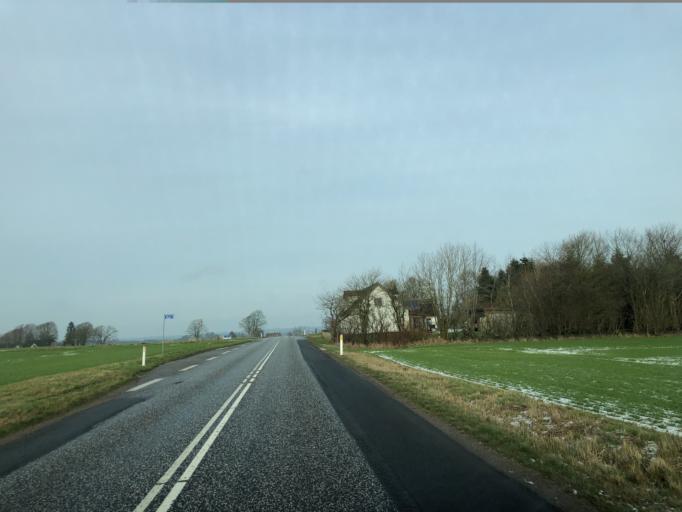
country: DK
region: Central Jutland
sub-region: Hedensted Kommune
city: Torring
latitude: 55.8195
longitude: 9.4743
